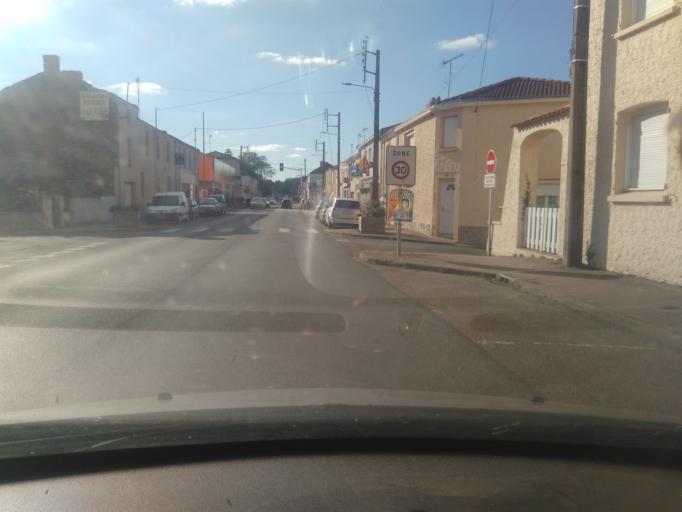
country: FR
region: Pays de la Loire
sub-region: Departement de la Vendee
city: Saint-Florent-des-Bois
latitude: 46.5928
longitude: -1.3146
